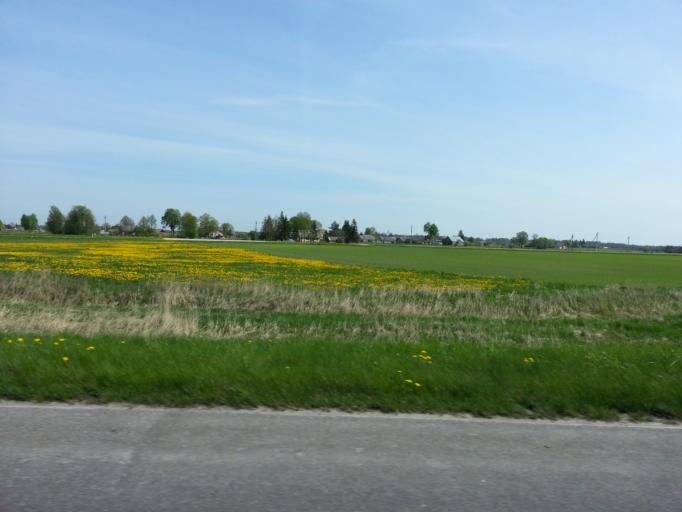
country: LT
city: Ramygala
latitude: 55.5517
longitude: 24.5195
